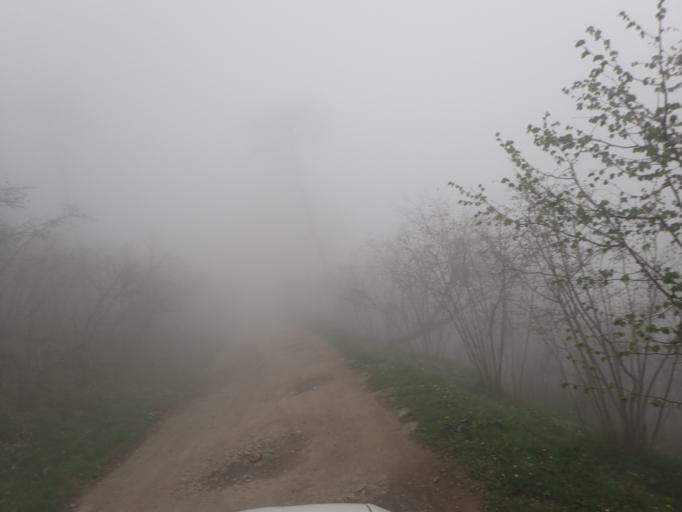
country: TR
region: Ordu
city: Korgan
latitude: 40.7801
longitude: 37.2899
